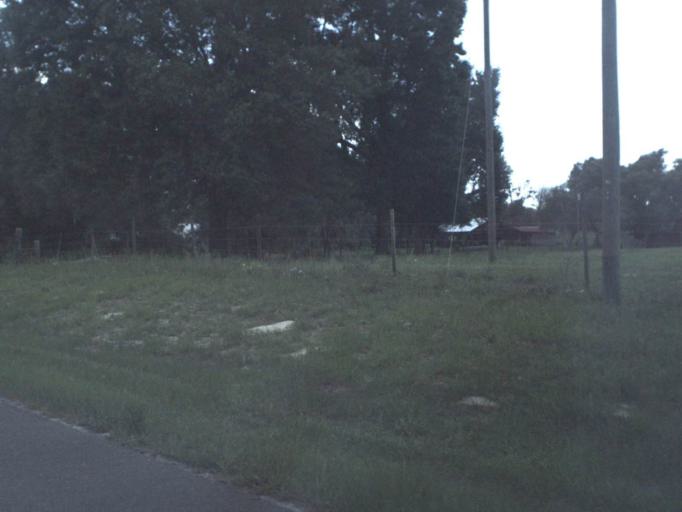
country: US
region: Florida
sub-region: Gilchrist County
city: Trenton
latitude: 29.7268
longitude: -82.7463
